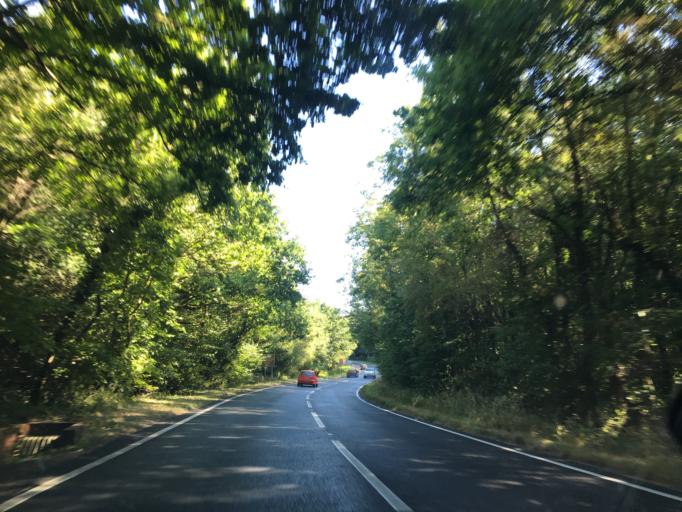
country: GB
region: England
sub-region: Isle of Wight
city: Brading
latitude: 50.7023
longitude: -1.1466
